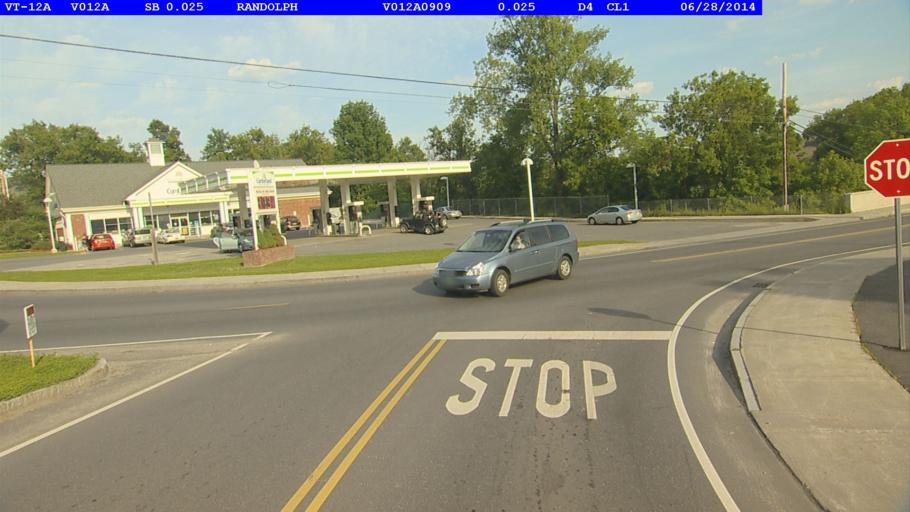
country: US
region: Vermont
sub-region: Orange County
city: Randolph
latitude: 43.9275
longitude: -72.6662
